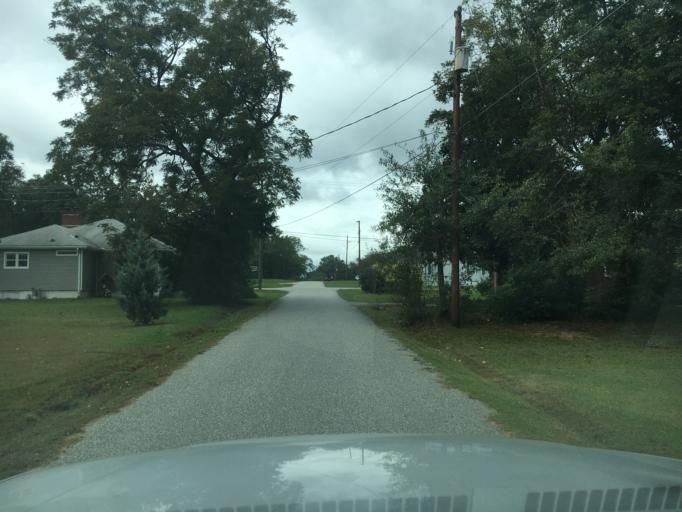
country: US
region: South Carolina
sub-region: Spartanburg County
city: Duncan
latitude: 34.8613
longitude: -82.1125
